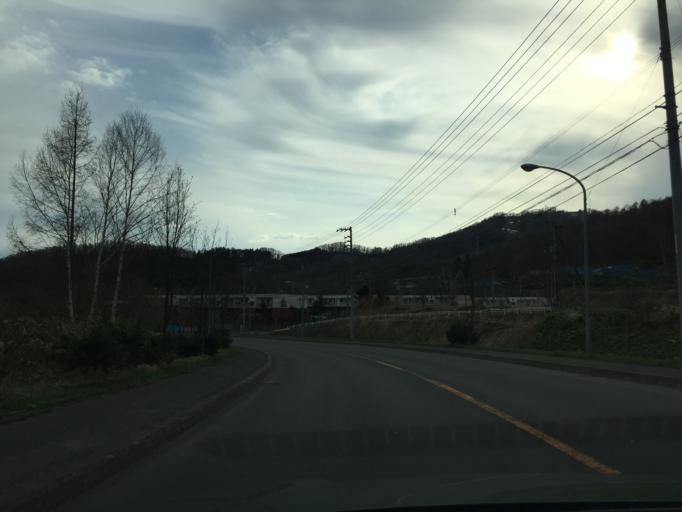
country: JP
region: Hokkaido
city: Utashinai
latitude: 43.5212
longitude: 142.0318
